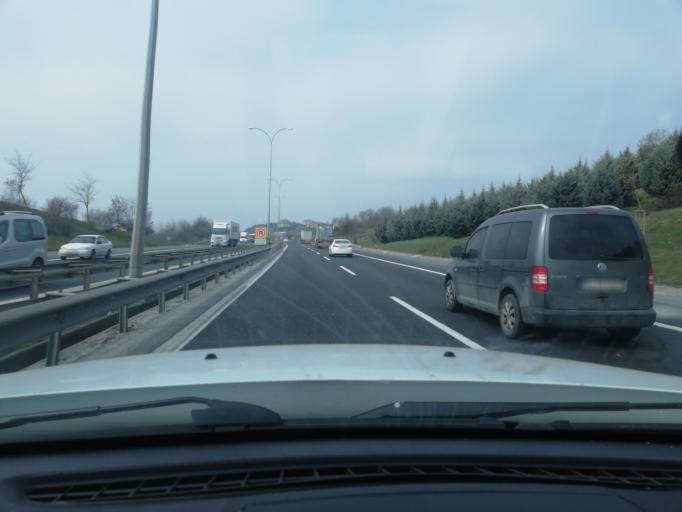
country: TR
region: Istanbul
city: Celaliye
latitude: 41.0546
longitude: 28.4276
